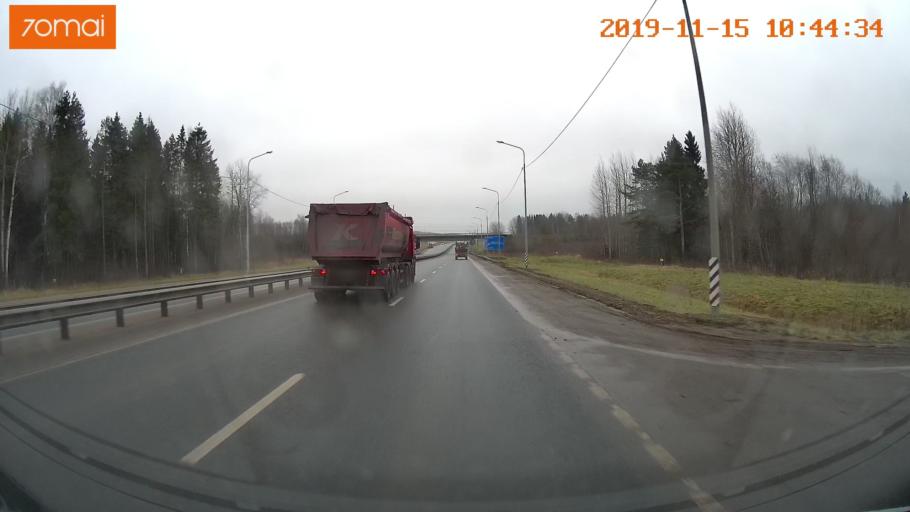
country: RU
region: Vologda
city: Sheksna
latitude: 59.2115
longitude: 38.5609
